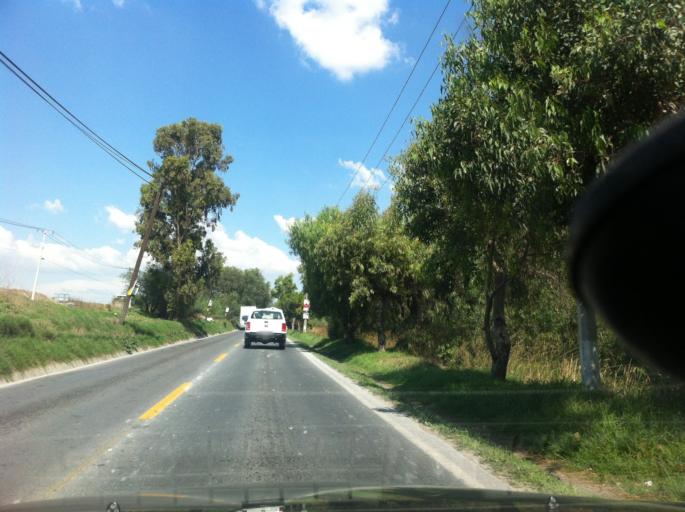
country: MX
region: Mexico
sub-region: Cuautitlan
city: La Providencia
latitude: 19.7621
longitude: -99.1257
